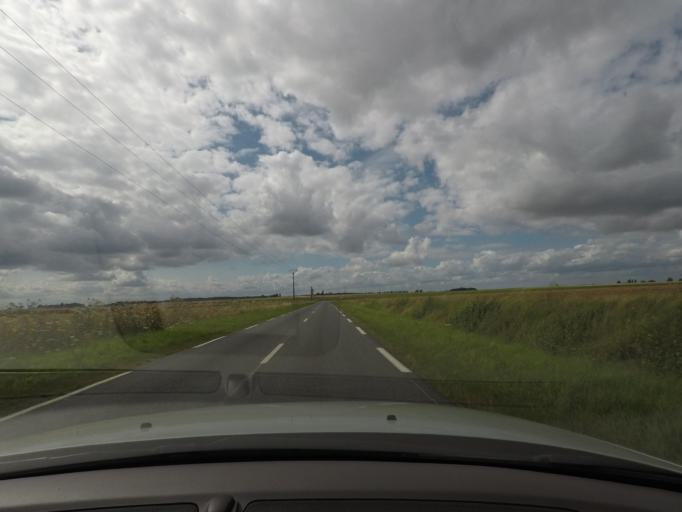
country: FR
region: Haute-Normandie
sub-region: Departement de l'Eure
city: Les Andelys
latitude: 49.2242
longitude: 1.4434
